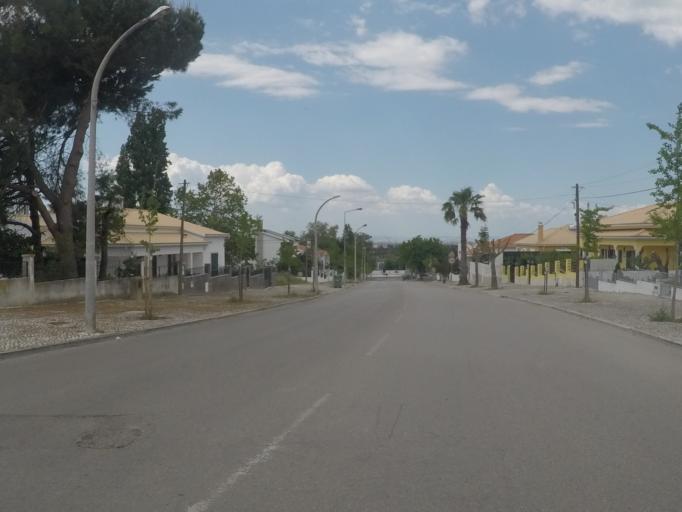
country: PT
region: Setubal
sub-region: Palmela
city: Quinta do Anjo
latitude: 38.5181
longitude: -9.0089
